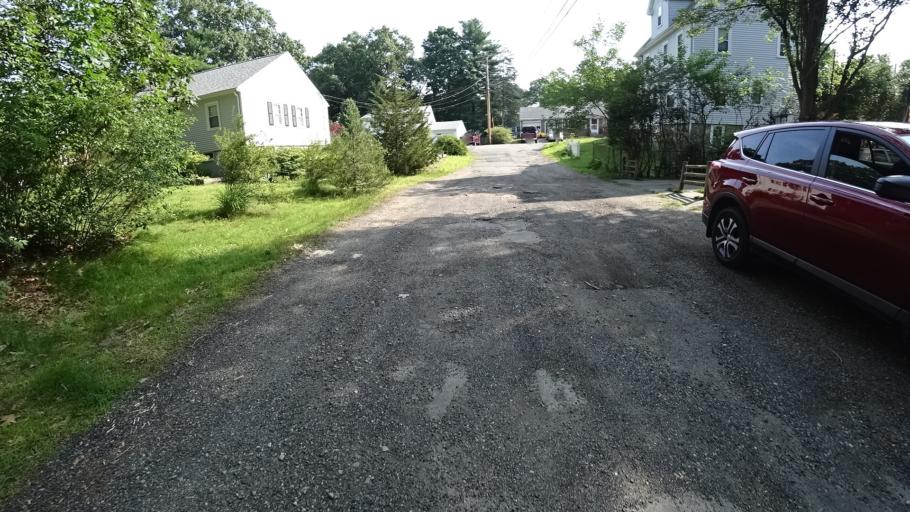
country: US
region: Massachusetts
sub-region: Norfolk County
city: Dedham
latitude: 42.2297
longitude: -71.1598
